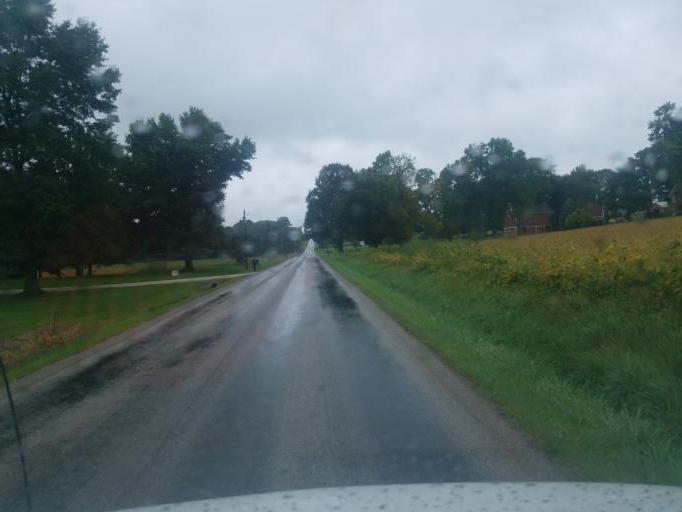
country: US
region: Ohio
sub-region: Wayne County
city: Creston
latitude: 40.9747
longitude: -81.9156
